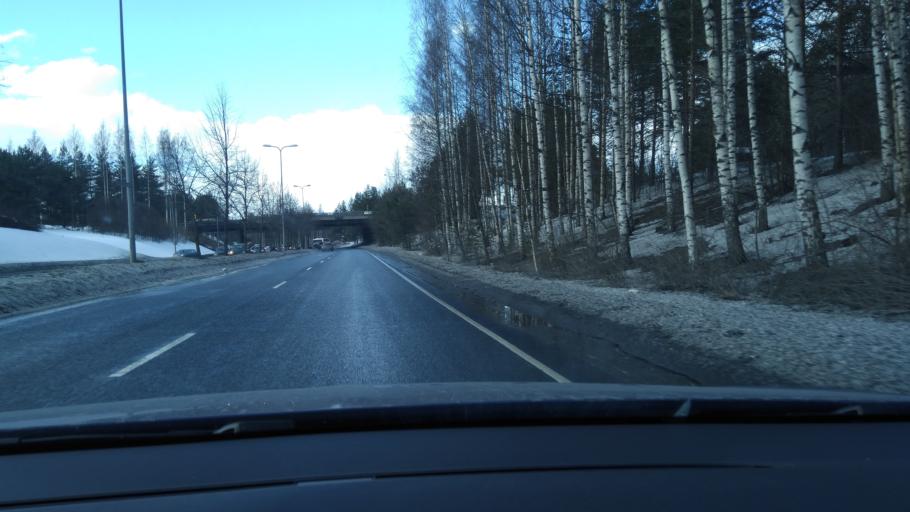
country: FI
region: Pirkanmaa
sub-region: Tampere
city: Tampere
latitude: 61.5010
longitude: 23.8076
